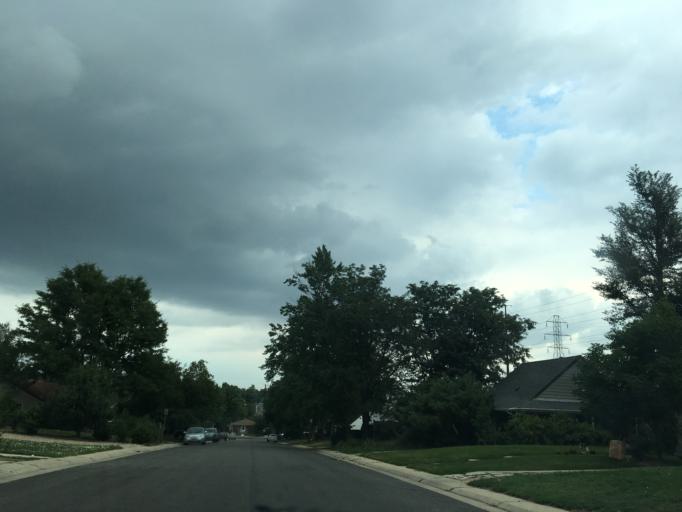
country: US
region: Colorado
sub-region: Arapahoe County
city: Englewood
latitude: 39.6876
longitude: -105.0070
